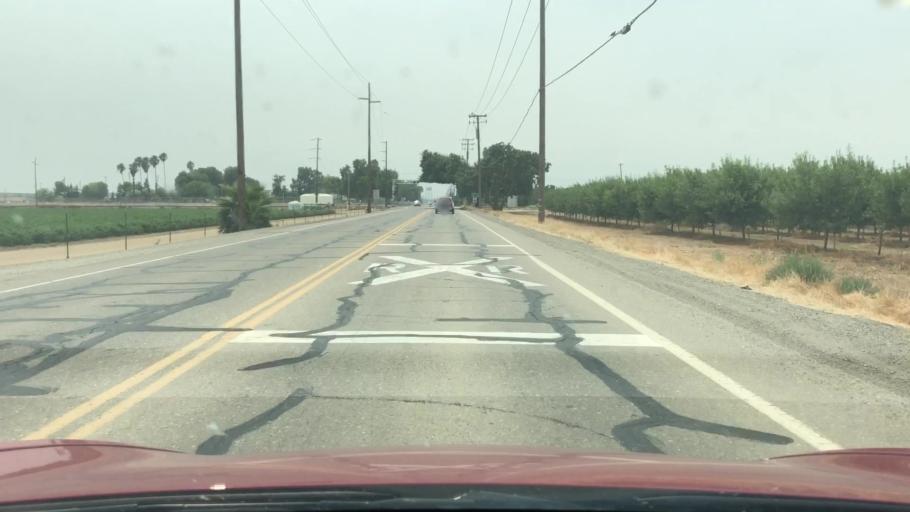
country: US
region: California
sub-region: San Joaquin County
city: Tracy
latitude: 37.7272
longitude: -121.3983
